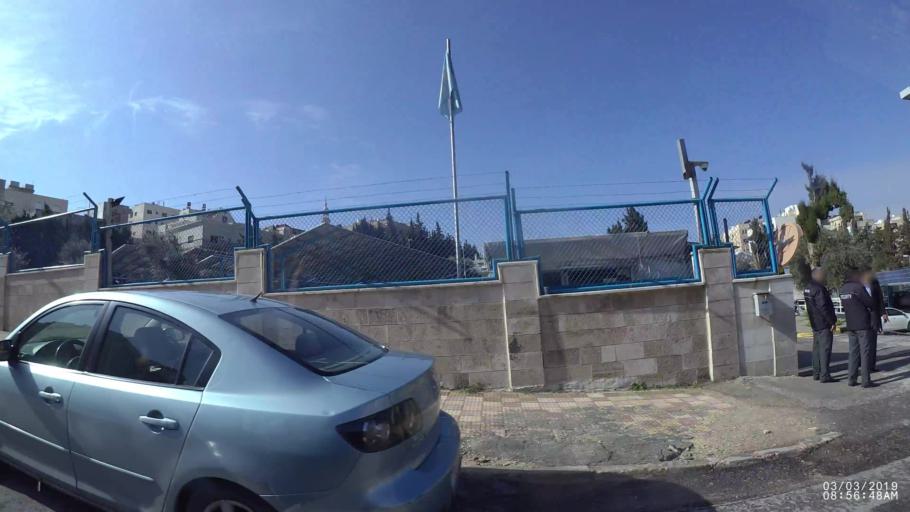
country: JO
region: Amman
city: Al Jubayhah
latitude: 32.0032
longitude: 35.8824
